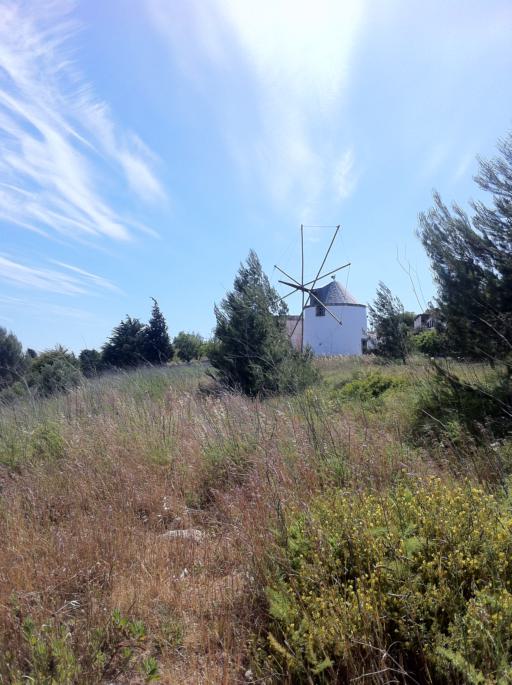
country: PT
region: Setubal
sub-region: Setubal
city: Setubal
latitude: 38.5202
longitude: -8.9122
